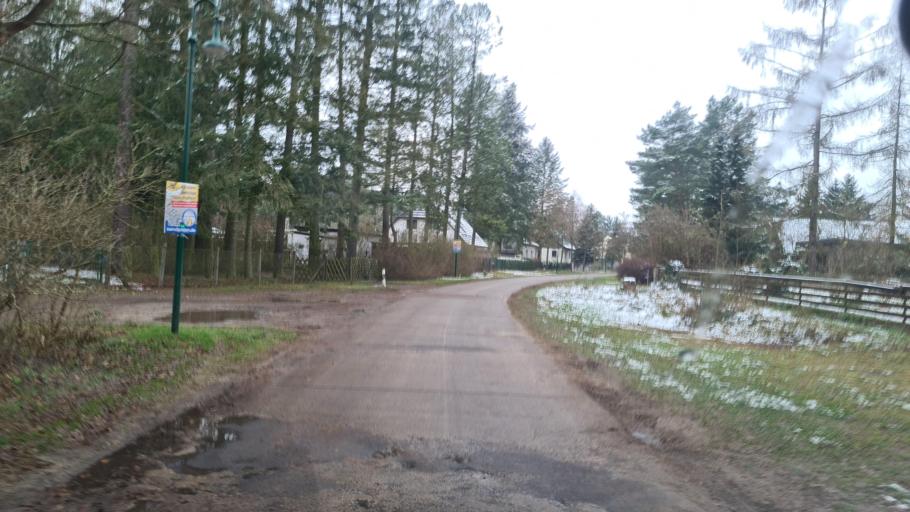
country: DE
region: Brandenburg
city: Rehfelde
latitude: 52.4556
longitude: 13.9122
